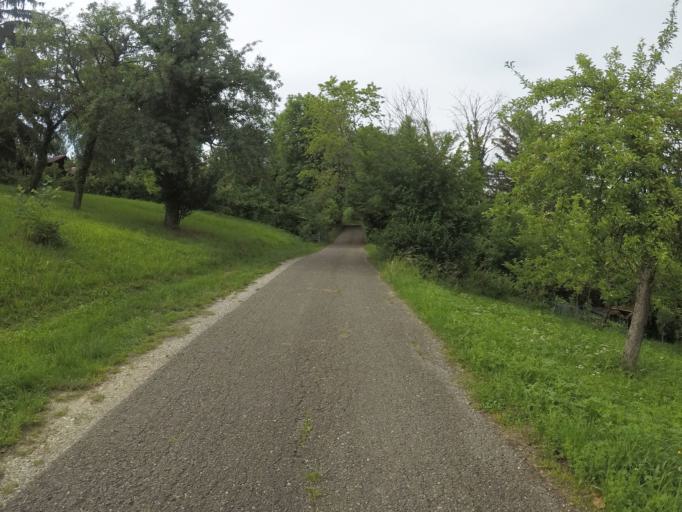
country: DE
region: Baden-Wuerttemberg
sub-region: Tuebingen Region
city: Pfullingen
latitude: 48.4722
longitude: 9.2157
